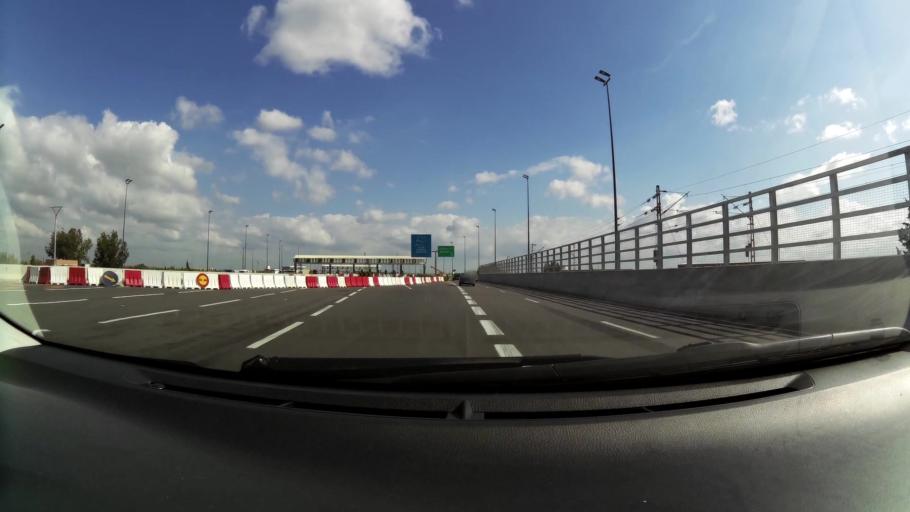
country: MA
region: Chaouia-Ouardigha
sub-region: Settat Province
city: Berrechid
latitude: 33.3224
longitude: -7.6057
